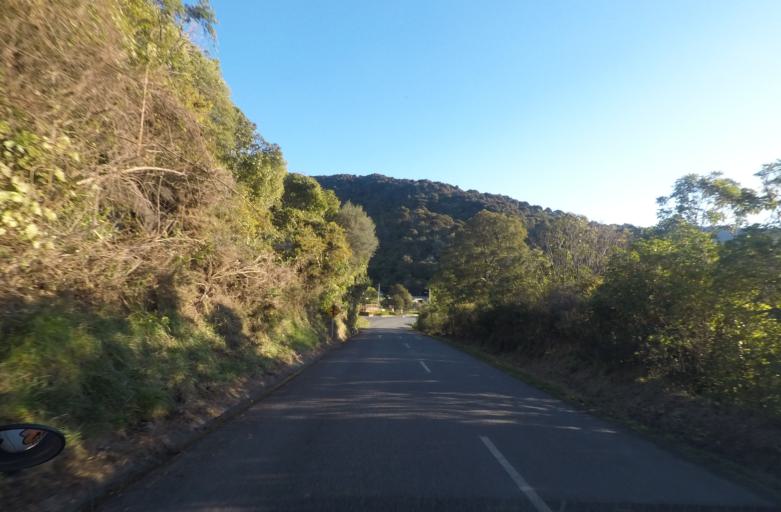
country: NZ
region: Marlborough
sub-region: Marlborough District
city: Picton
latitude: -41.2701
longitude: 173.9425
